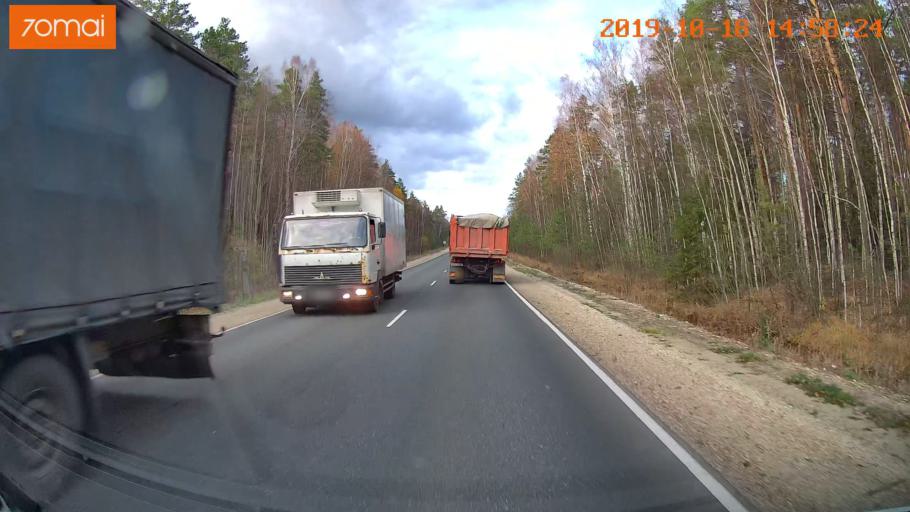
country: RU
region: Vladimir
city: Kurlovo
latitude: 55.4901
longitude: 40.5773
